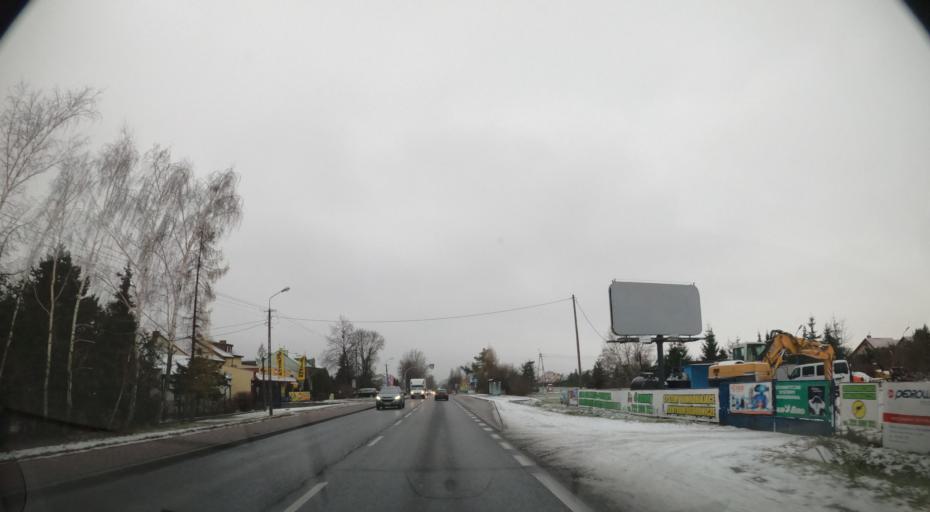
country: PL
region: Masovian Voivodeship
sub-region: Plock
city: Plock
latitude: 52.5321
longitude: 19.7734
